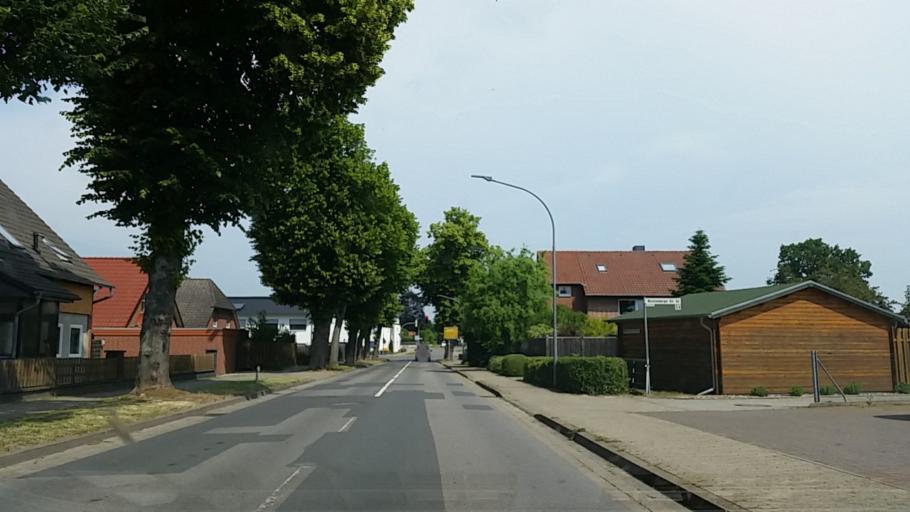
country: DE
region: Lower Saxony
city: Calberlah
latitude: 52.4202
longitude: 10.6233
